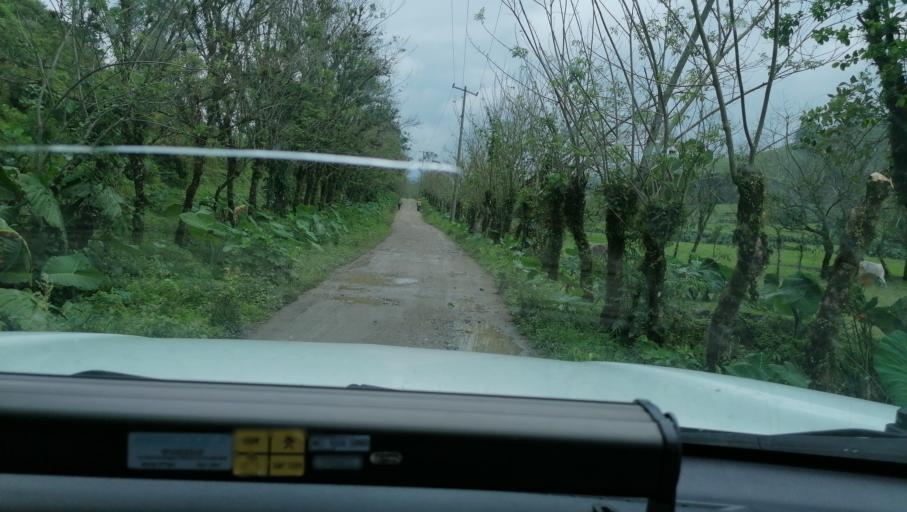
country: MX
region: Chiapas
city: Ixtacomitan
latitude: 17.3519
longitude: -93.1596
